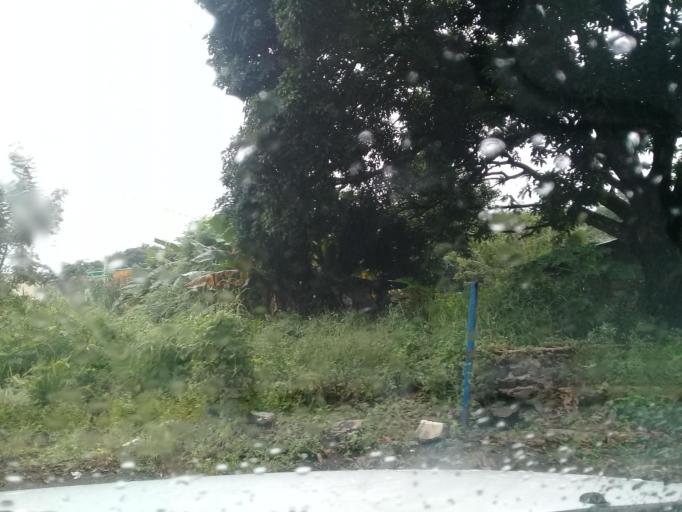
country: MX
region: Veracruz
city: San Andres Tuxtla
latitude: 18.4374
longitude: -95.1930
